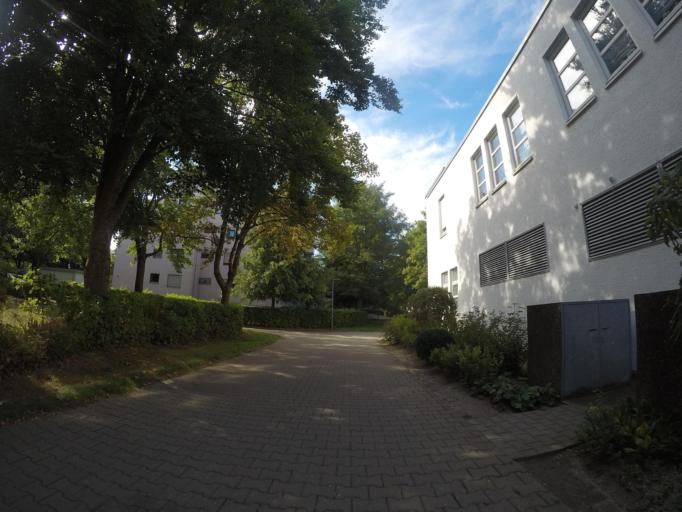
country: DE
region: Baden-Wuerttemberg
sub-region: Tuebingen Region
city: Ulm
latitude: 48.3508
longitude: 9.9749
